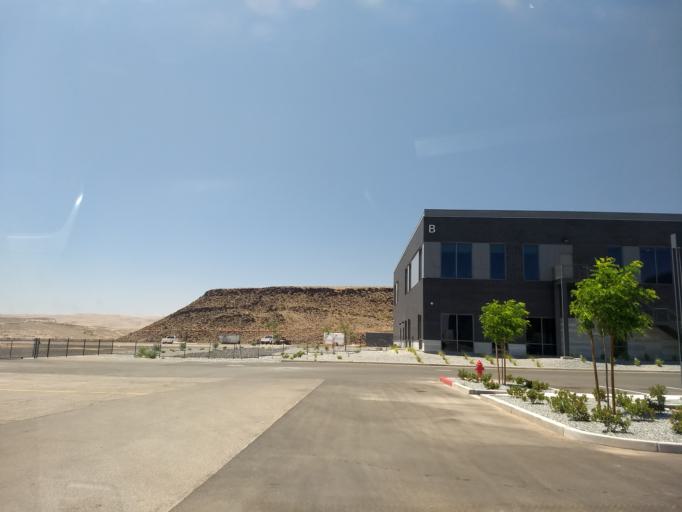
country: US
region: Utah
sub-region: Washington County
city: Saint George
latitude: 37.0979
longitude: -113.5921
